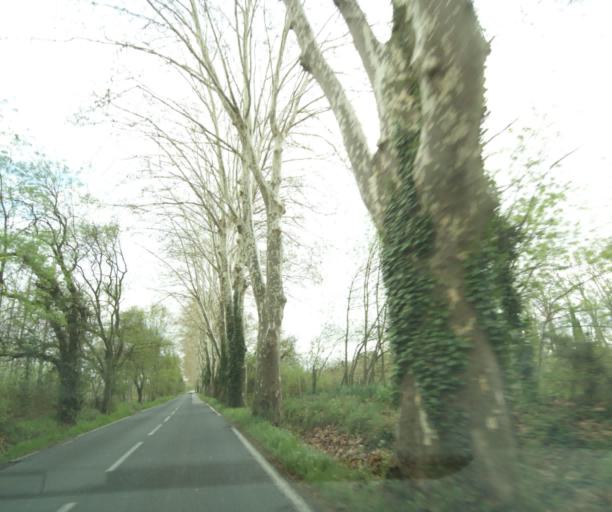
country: FR
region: Languedoc-Roussillon
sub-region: Departement de l'Herault
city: Laverune
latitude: 43.5905
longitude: 3.8185
